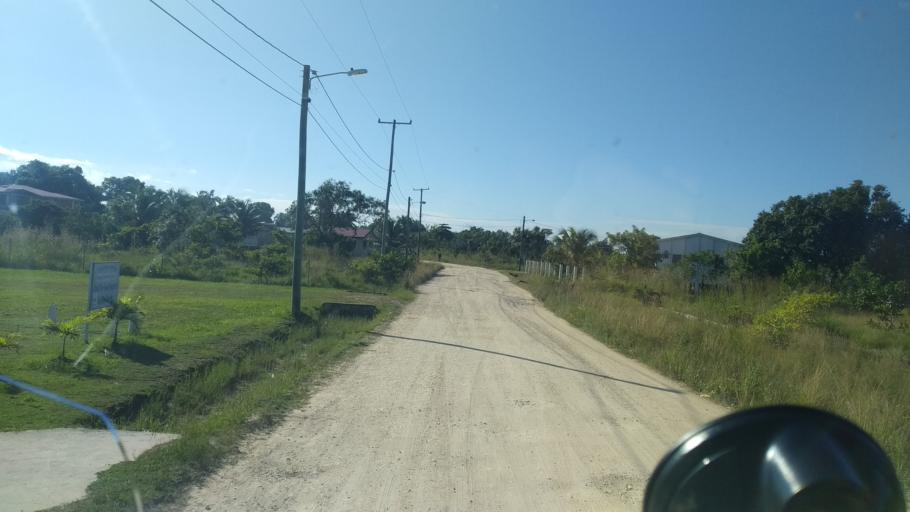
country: BZ
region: Belize
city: Belize City
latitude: 17.5528
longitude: -88.3261
